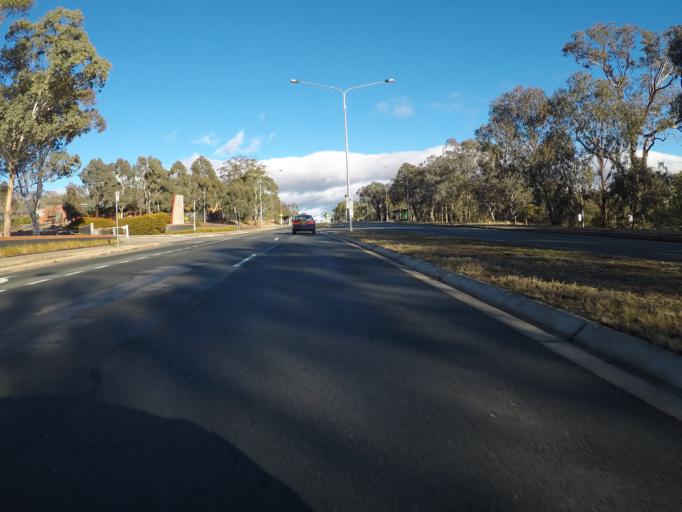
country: AU
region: Australian Capital Territory
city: Macquarie
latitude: -35.2425
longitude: 149.0872
